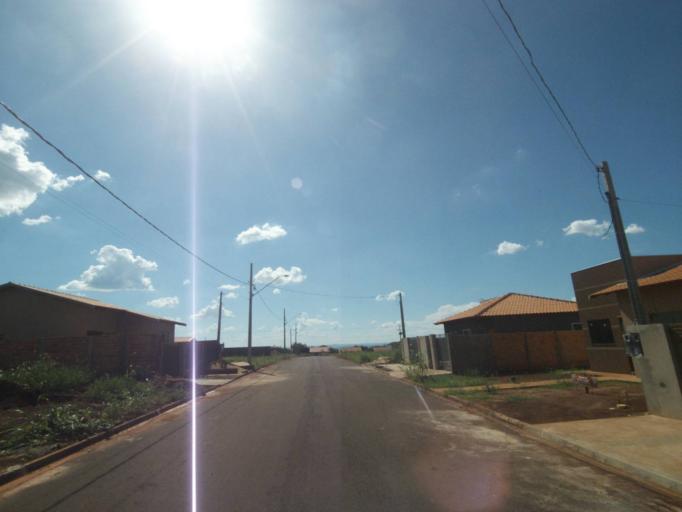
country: BR
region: Parana
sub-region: Sertanopolis
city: Sertanopolis
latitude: -23.0362
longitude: -50.8101
